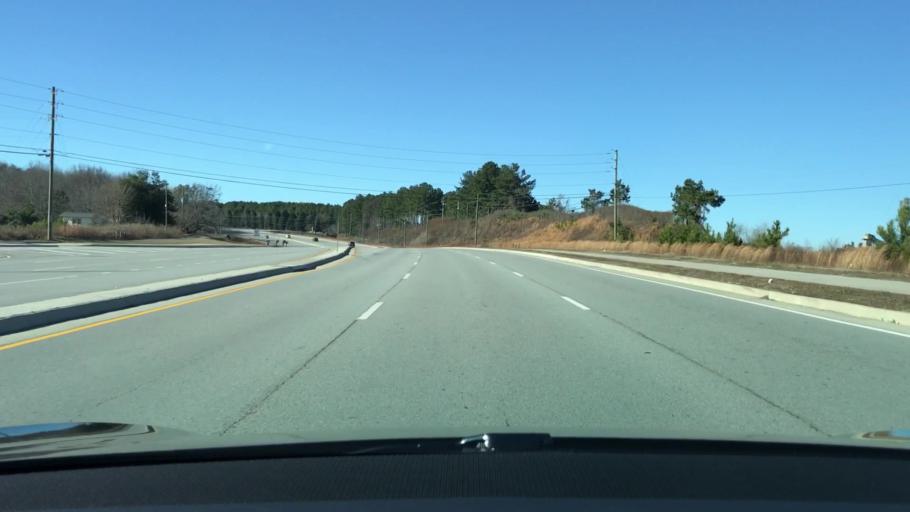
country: US
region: Georgia
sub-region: Hall County
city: Flowery Branch
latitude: 34.1280
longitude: -83.9229
